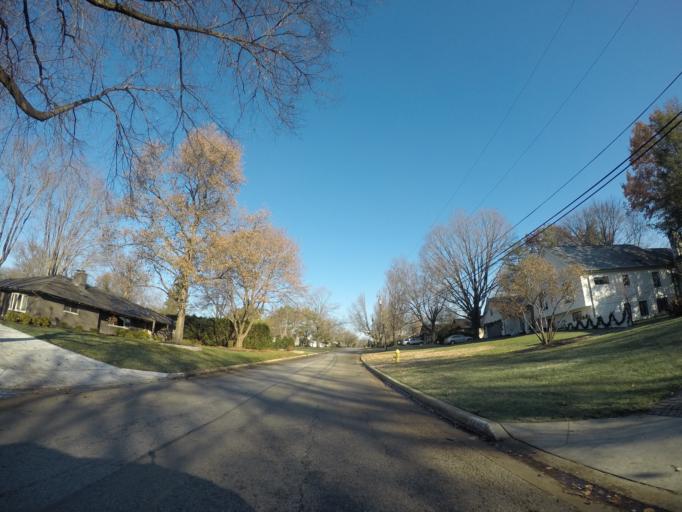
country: US
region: Ohio
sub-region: Franklin County
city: Upper Arlington
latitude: 40.0366
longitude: -83.0631
